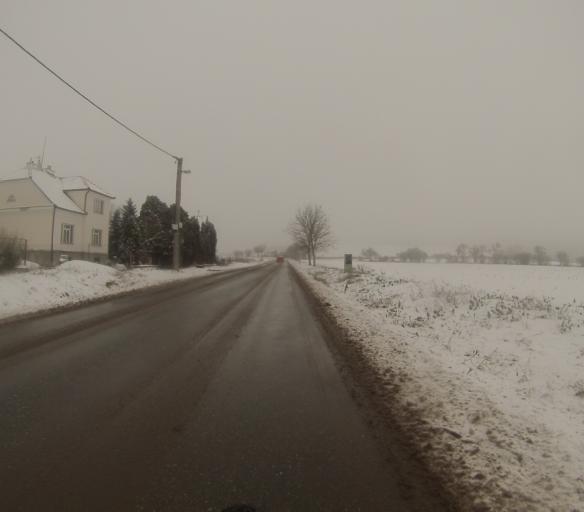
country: CZ
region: South Moravian
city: Ostopovice
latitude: 49.1625
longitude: 16.5286
